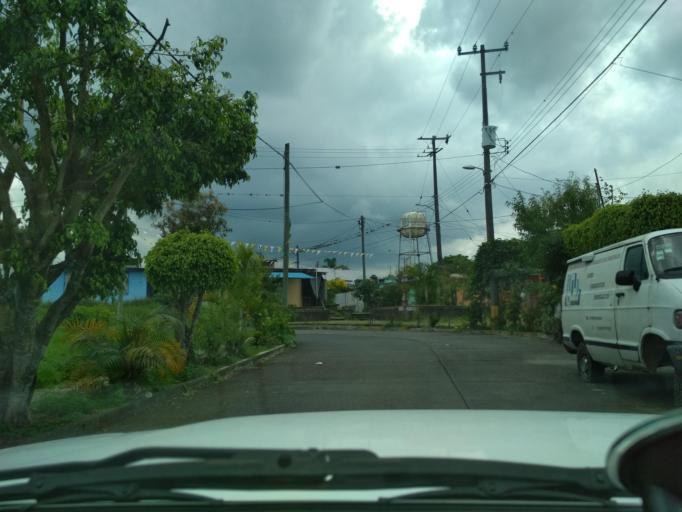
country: MX
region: Veracruz
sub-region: Cordoba
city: San Jose de Abajo [Unidad Habitacional]
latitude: 18.9207
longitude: -96.9634
